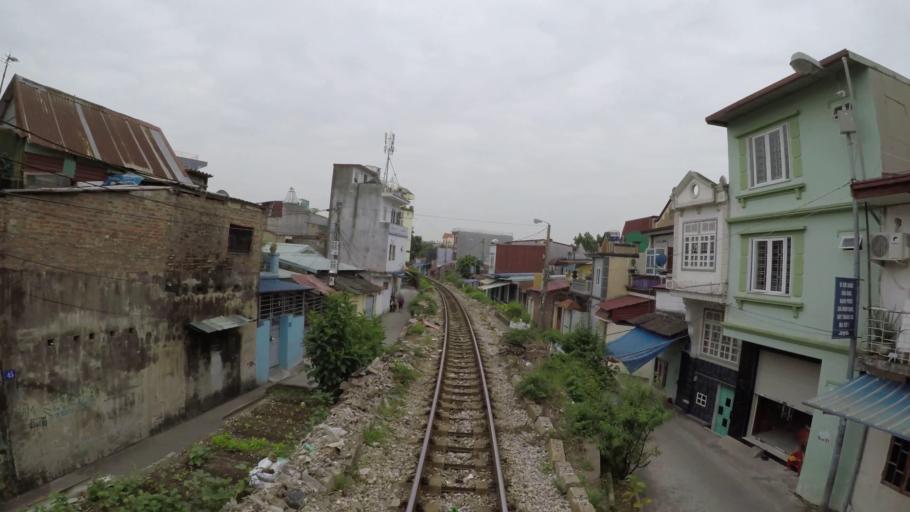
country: VN
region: Hai Phong
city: Haiphong
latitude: 20.8695
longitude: 106.6541
